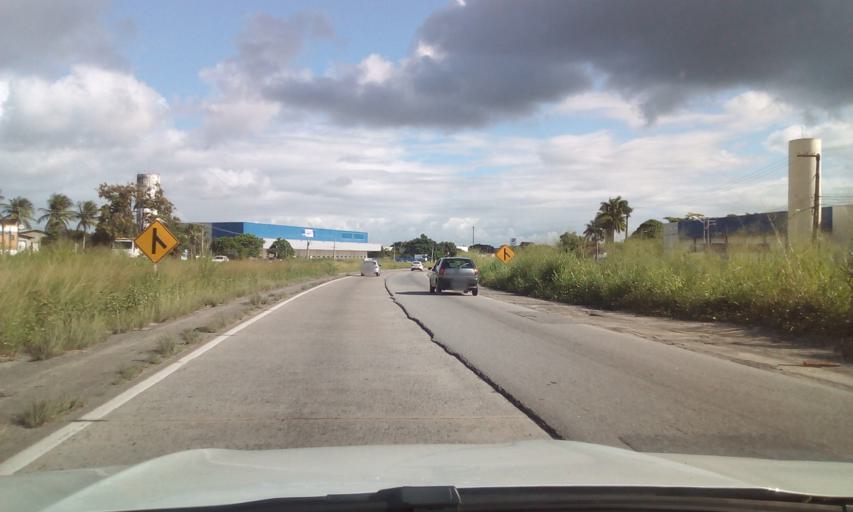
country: BR
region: Pernambuco
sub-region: Paulista
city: Paulista
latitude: -7.9596
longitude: -34.9125
